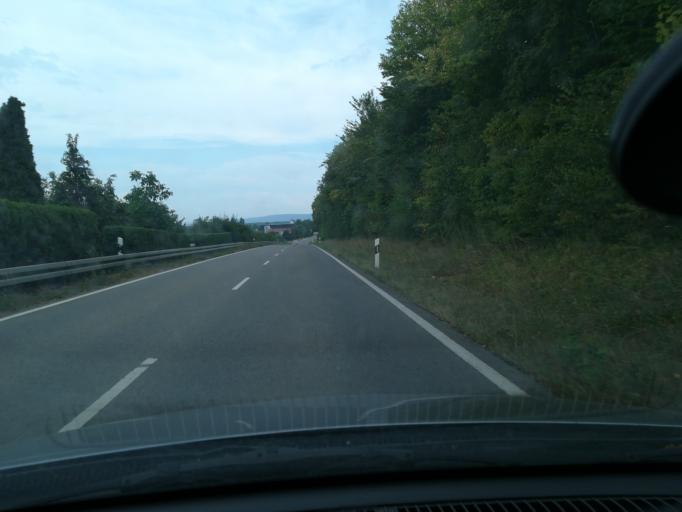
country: DE
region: Baden-Wuerttemberg
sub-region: Freiburg Region
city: Muhlhausen-Ehingen
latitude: 47.8069
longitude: 8.8195
